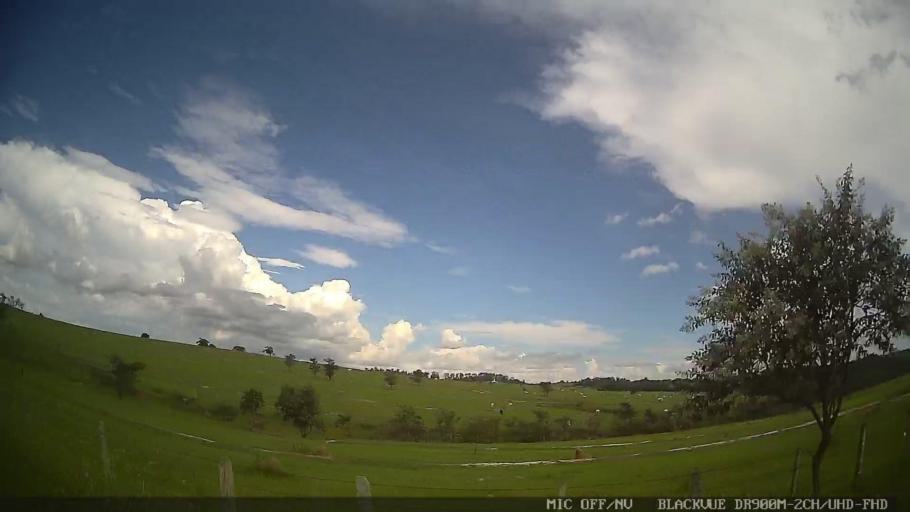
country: BR
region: Sao Paulo
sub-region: Conchas
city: Conchas
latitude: -22.9760
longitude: -47.9877
